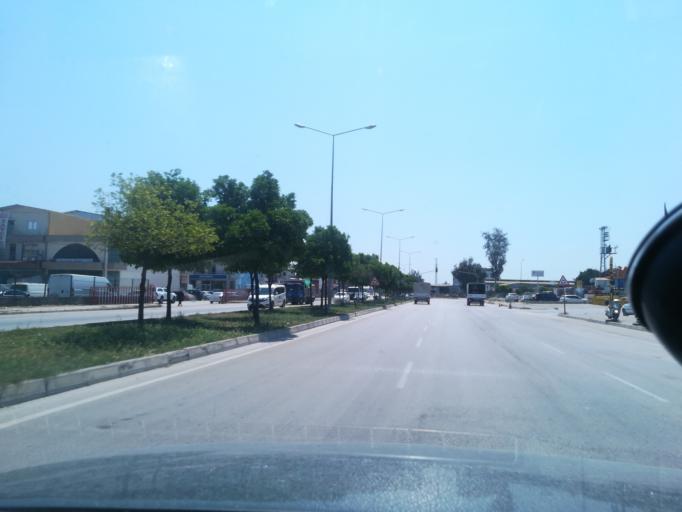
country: TR
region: Adana
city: Seyhan
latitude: 36.9926
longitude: 35.2523
